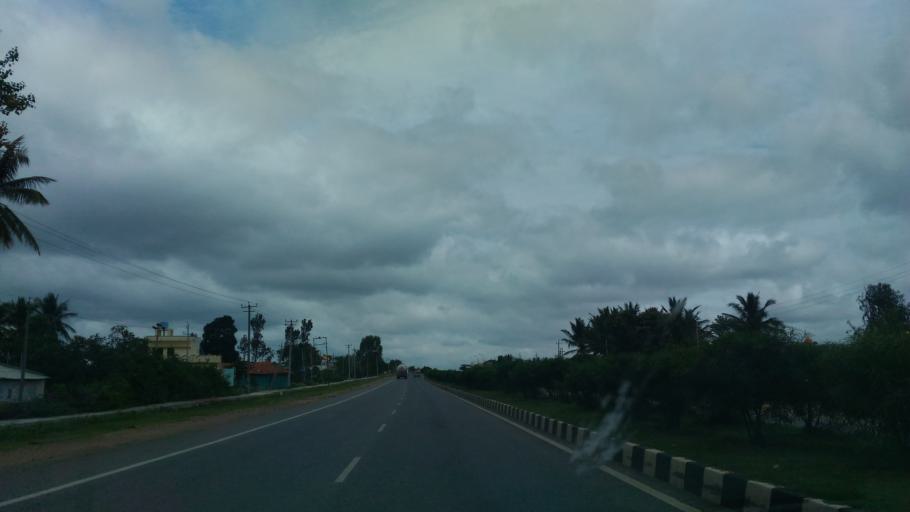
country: IN
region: Karnataka
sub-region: Hassan
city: Channarayapatna
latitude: 12.9745
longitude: 76.2618
